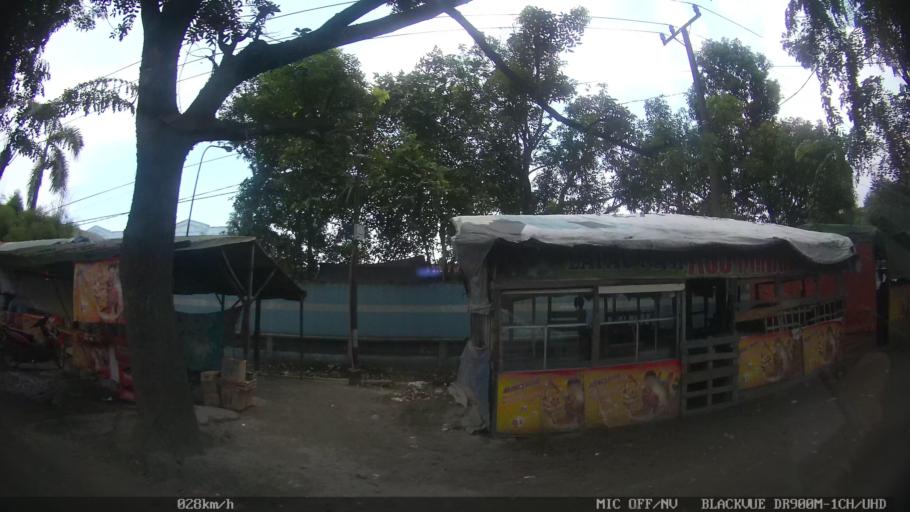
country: ID
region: North Sumatra
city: Labuhan Deli
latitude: 3.6766
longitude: 98.6852
